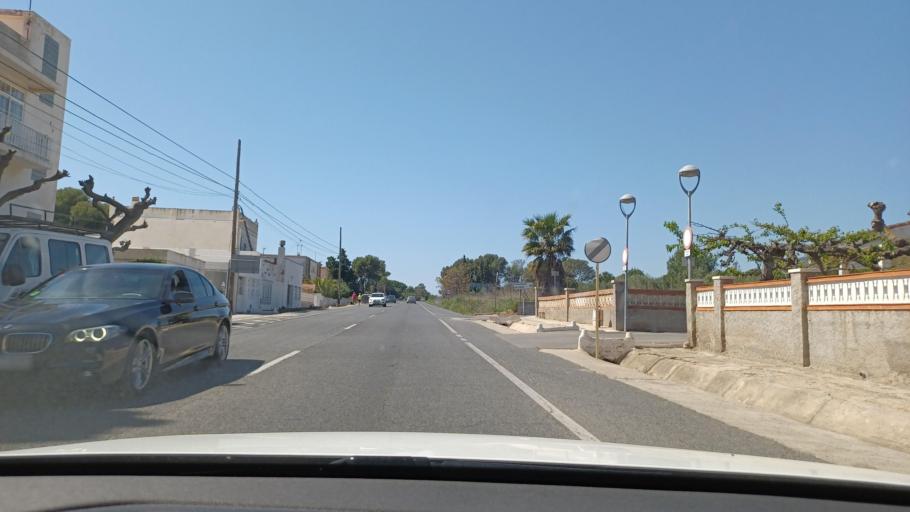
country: ES
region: Catalonia
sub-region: Provincia de Tarragona
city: Sant Carles de la Rapita
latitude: 40.6043
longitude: 0.5802
